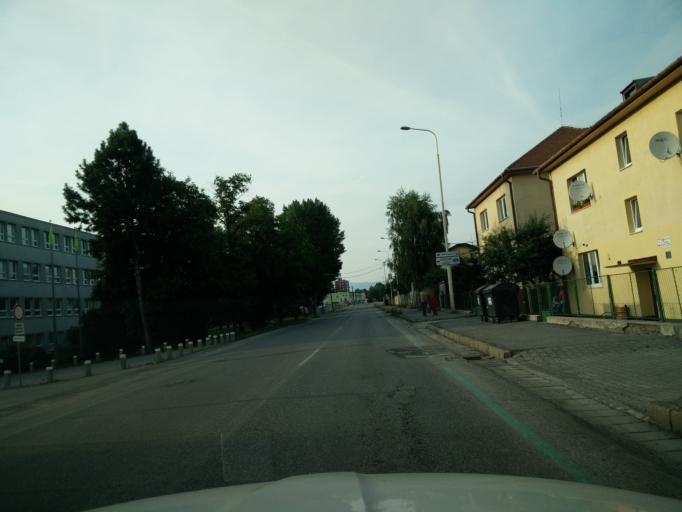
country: SK
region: Nitriansky
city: Prievidza
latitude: 48.7650
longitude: 18.6184
